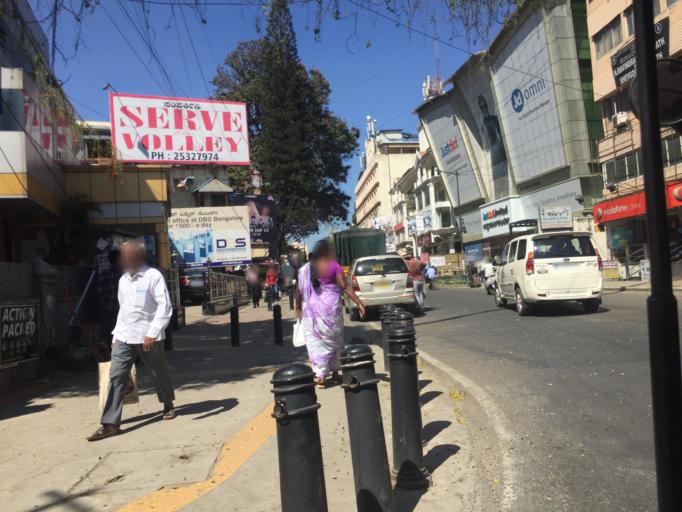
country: IN
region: Karnataka
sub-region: Bangalore Urban
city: Bangalore
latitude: 12.9845
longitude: 77.5970
